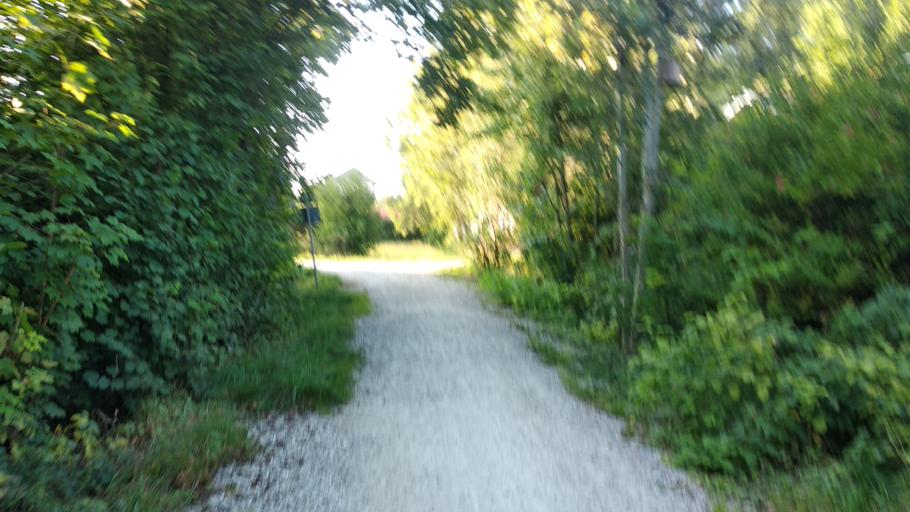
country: DE
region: Bavaria
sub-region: Upper Bavaria
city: Isen
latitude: 48.2121
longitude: 12.0612
